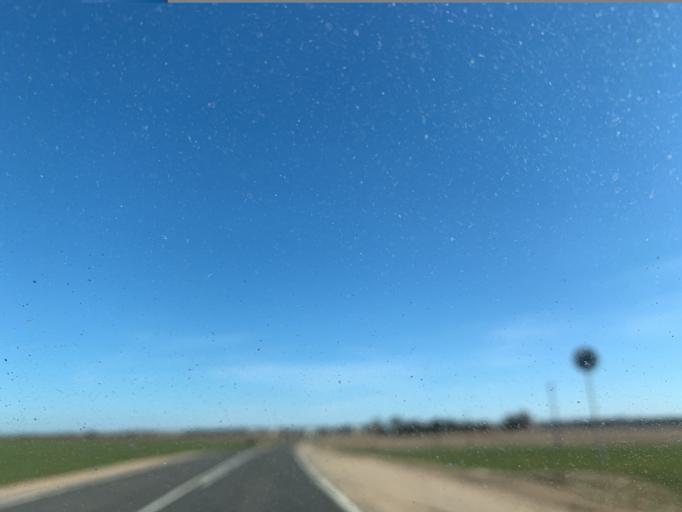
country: BY
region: Minsk
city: Nyasvizh
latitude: 53.2243
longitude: 26.7097
